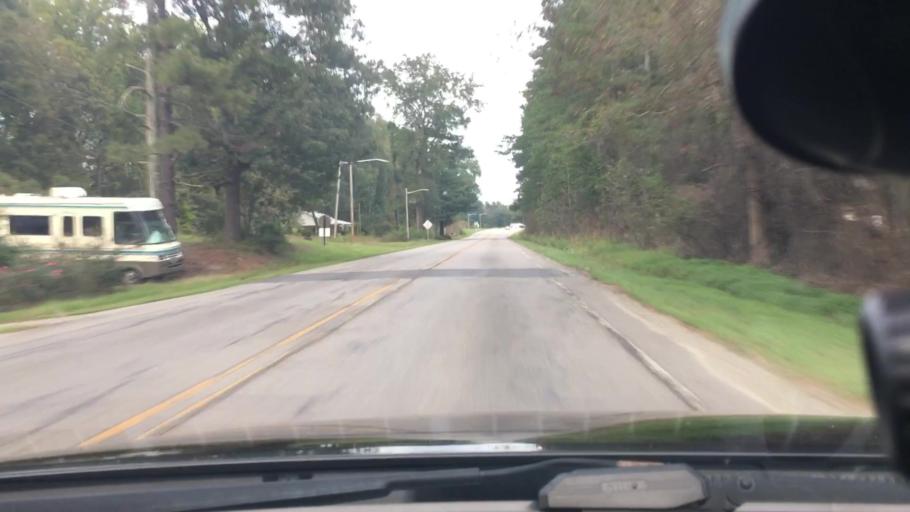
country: US
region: North Carolina
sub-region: Moore County
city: Carthage
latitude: 35.3458
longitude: -79.3867
